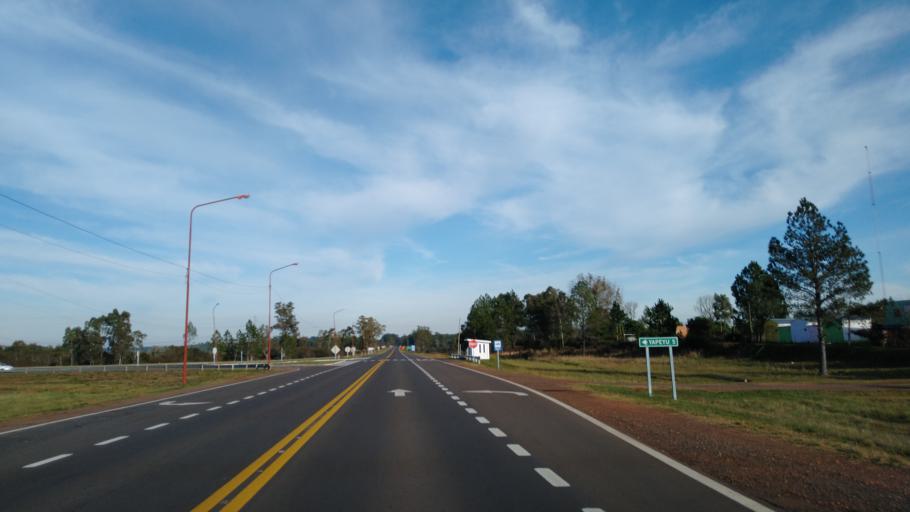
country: AR
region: Corrientes
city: Yapeyu
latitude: -29.4220
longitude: -56.8449
